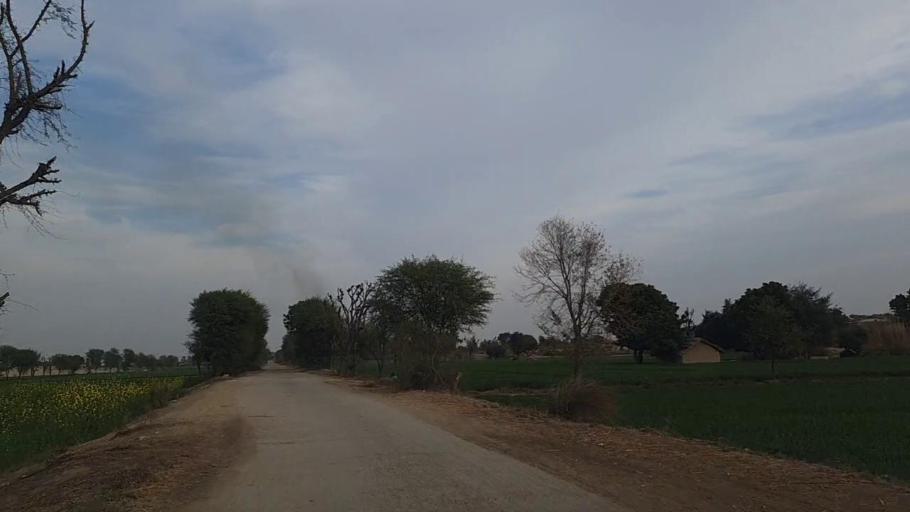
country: PK
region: Sindh
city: Daur
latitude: 26.5280
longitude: 68.4261
